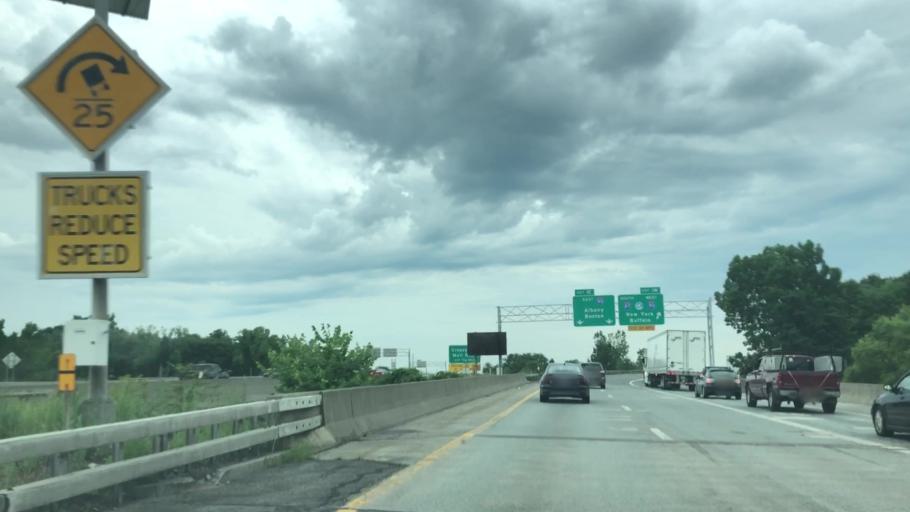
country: US
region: New York
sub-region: Albany County
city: McKownville
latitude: 42.6986
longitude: -73.8369
